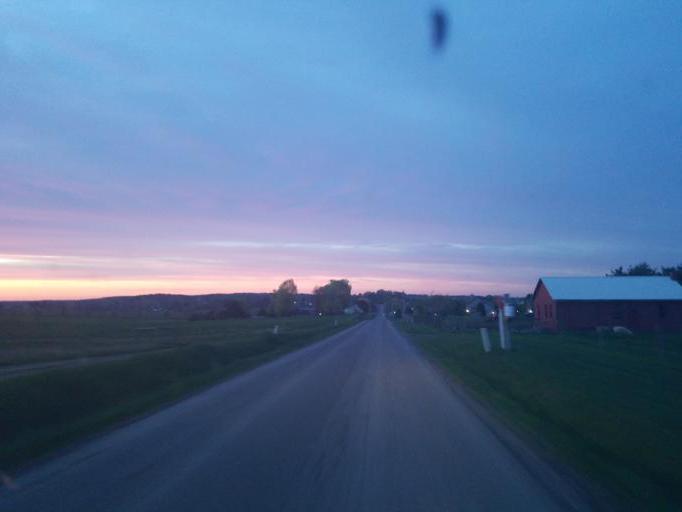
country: US
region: Ohio
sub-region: Wayne County
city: Apple Creek
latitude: 40.7311
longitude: -81.8241
